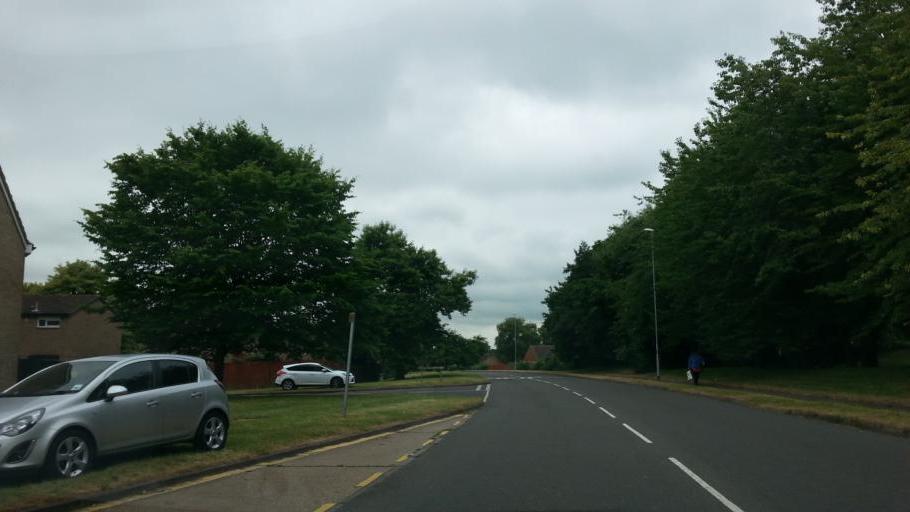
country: GB
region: England
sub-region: Northamptonshire
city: Northampton
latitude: 52.2678
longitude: -0.8209
